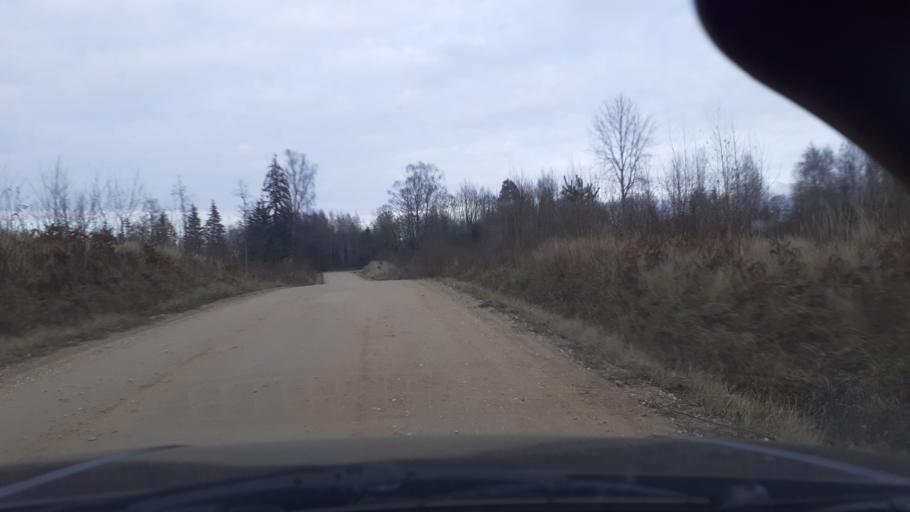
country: LV
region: Alsunga
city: Alsunga
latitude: 56.9649
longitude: 21.6547
